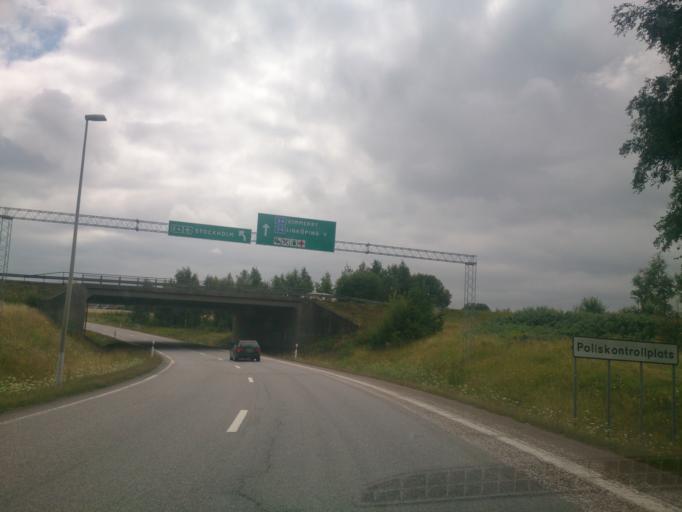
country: SE
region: OEstergoetland
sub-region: Linkopings Kommun
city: Malmslatt
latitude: 58.4351
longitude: 15.5261
